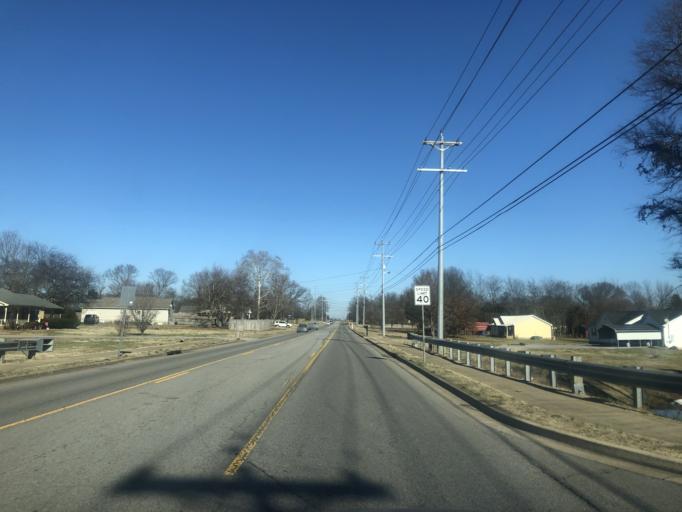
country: US
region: Tennessee
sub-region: Rutherford County
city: Smyrna
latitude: 35.8999
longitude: -86.4760
